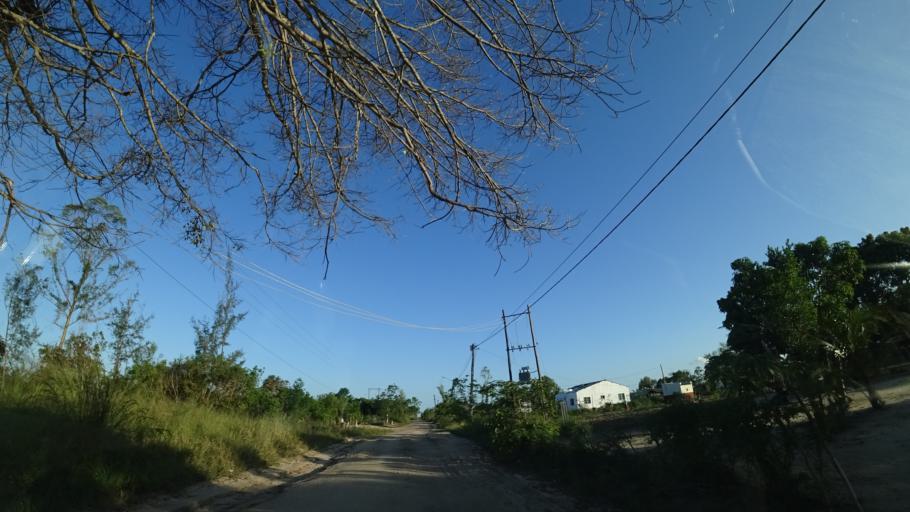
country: MZ
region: Sofala
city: Dondo
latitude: -19.3950
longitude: 34.7088
